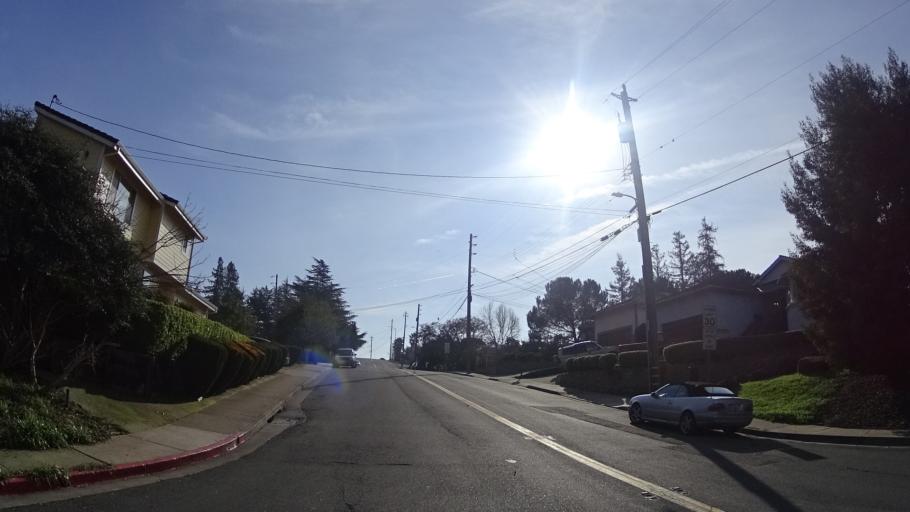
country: US
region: California
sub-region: Alameda County
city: Fairview
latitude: 37.6893
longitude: -122.0549
